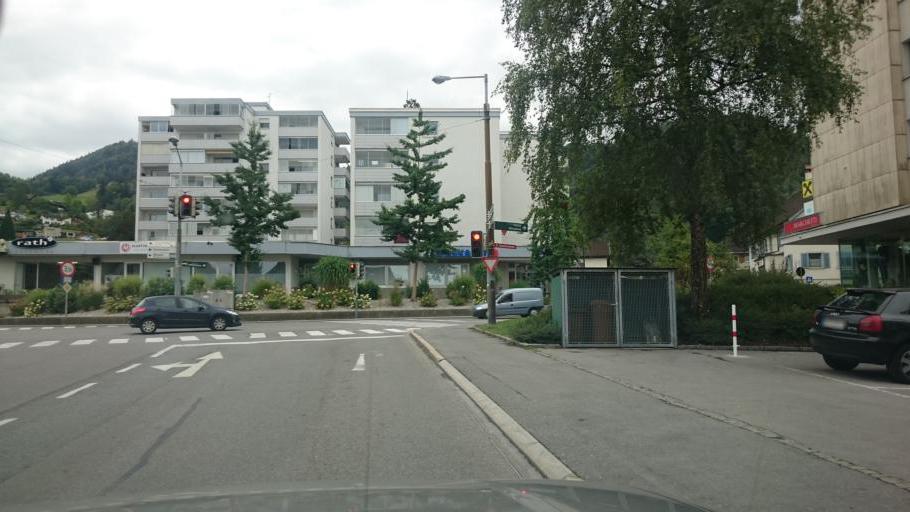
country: AT
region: Vorarlberg
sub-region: Politischer Bezirk Bregenz
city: Schwarzach
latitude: 47.4310
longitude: 9.7554
